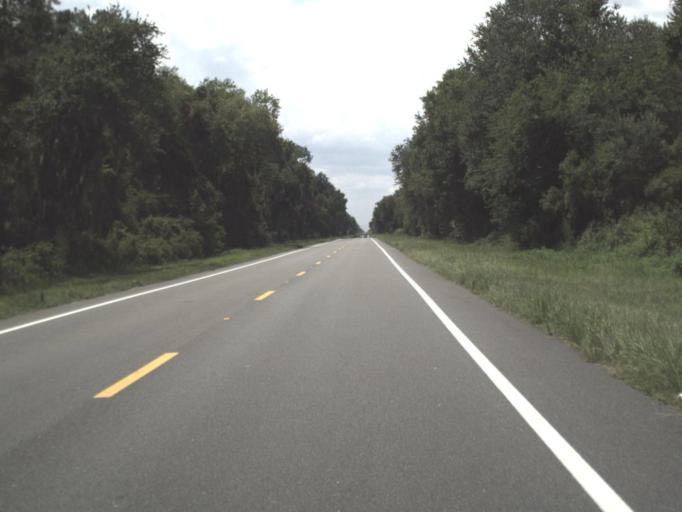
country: US
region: Florida
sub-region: Hamilton County
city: Jasper
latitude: 30.4223
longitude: -82.8577
